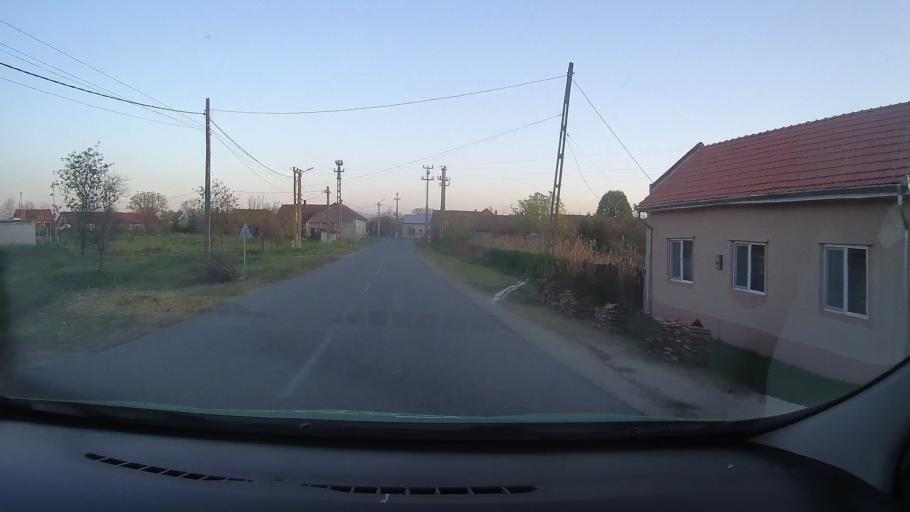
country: RO
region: Timis
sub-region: Comuna Manastiur
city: Manastiur
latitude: 45.8342
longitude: 22.0672
